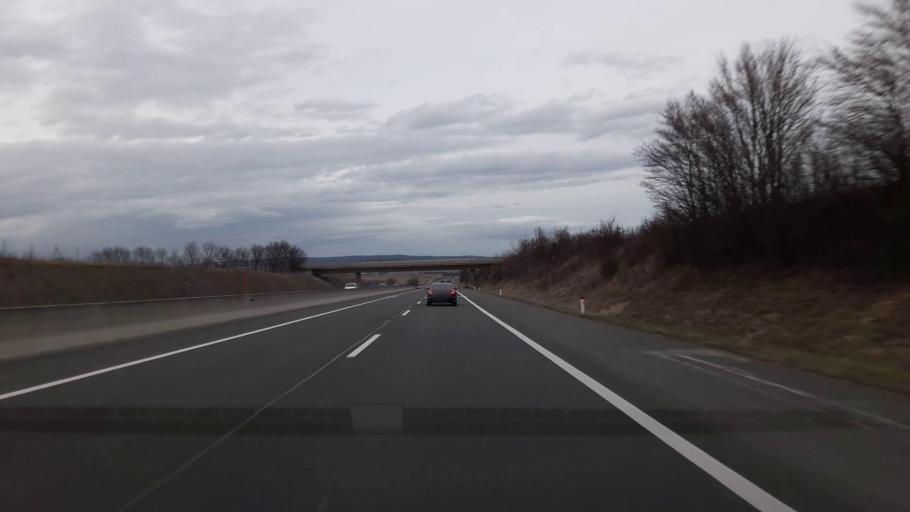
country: AT
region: Burgenland
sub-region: Politischer Bezirk Mattersburg
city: Krensdorf
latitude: 47.7747
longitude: 16.4318
